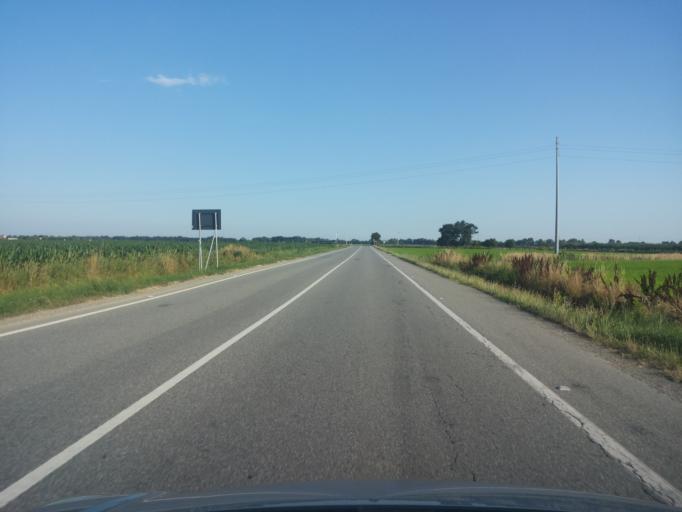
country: IT
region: Piedmont
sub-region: Provincia di Vercelli
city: Collobiano
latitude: 45.4061
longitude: 8.3281
